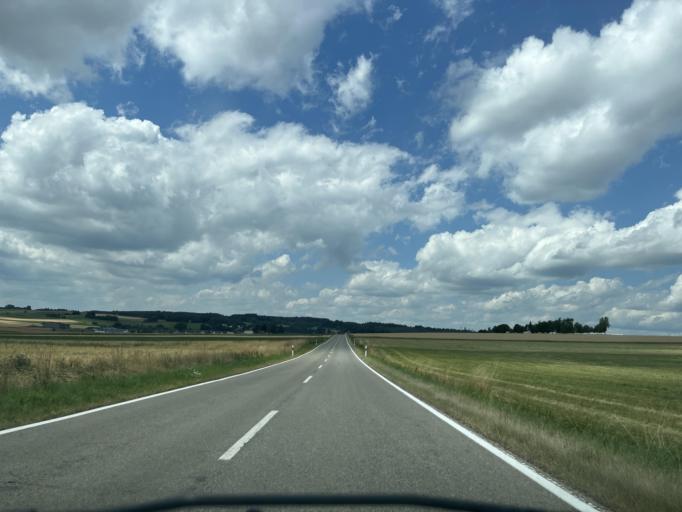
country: DE
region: Baden-Wuerttemberg
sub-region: Tuebingen Region
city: Leibertingen
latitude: 48.0424
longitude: 9.0309
